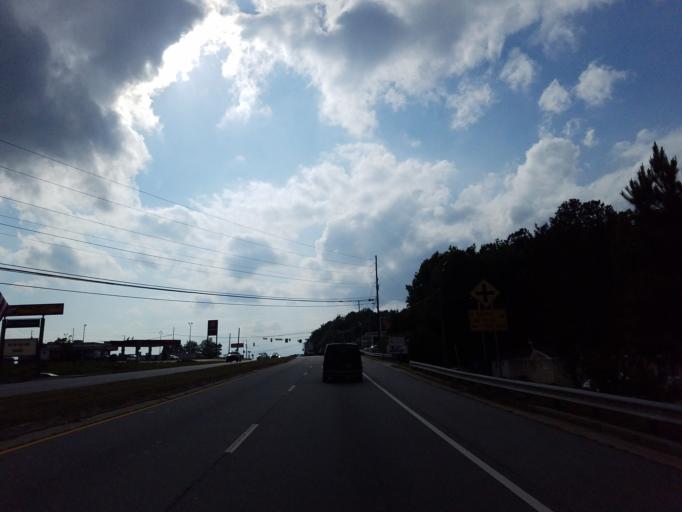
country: US
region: Georgia
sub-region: Douglas County
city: Douglasville
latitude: 33.7455
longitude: -84.6927
